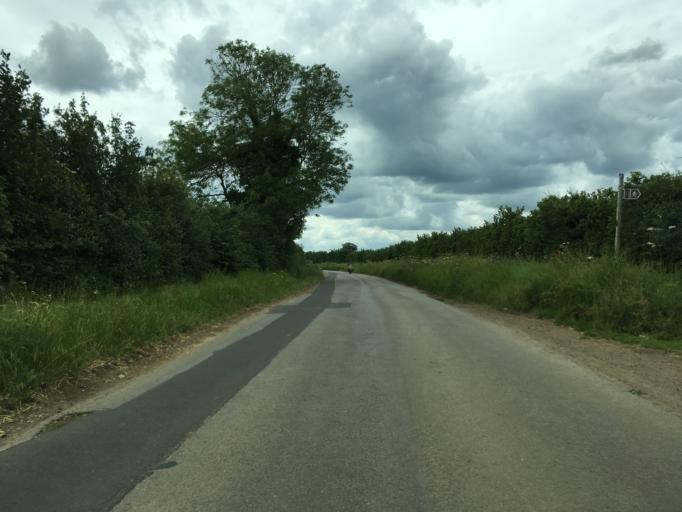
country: GB
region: England
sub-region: Wiltshire
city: Norton
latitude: 51.5318
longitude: -2.1587
